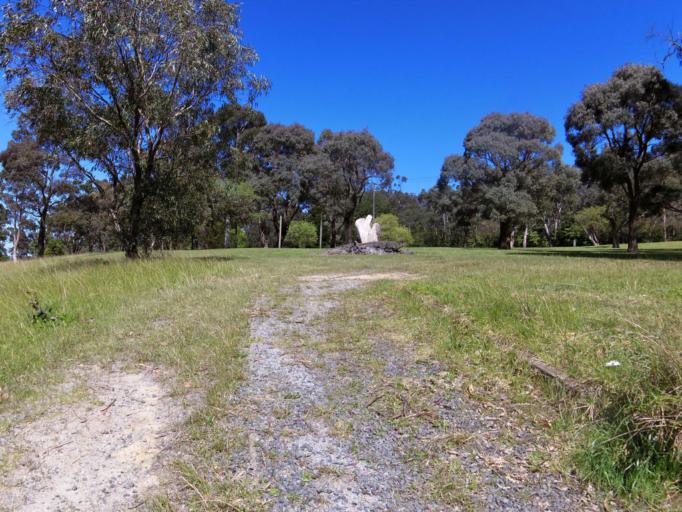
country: AU
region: Victoria
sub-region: Latrobe
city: Morwell
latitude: -38.1786
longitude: 146.3401
